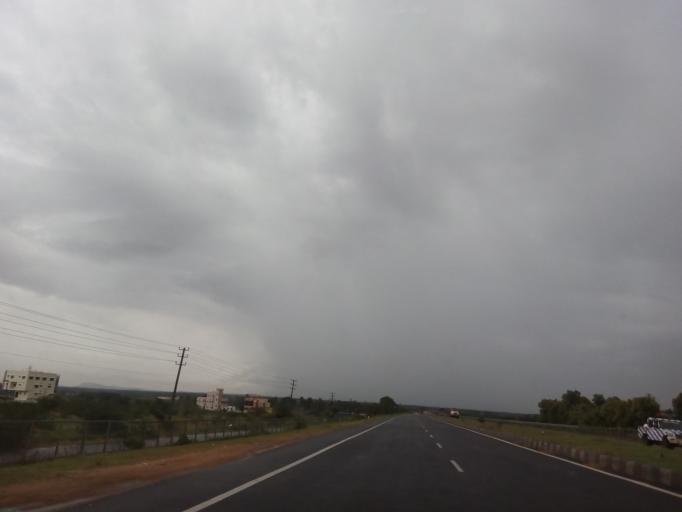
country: IN
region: Karnataka
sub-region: Davanagere
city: Harihar
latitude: 14.4323
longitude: 75.9368
